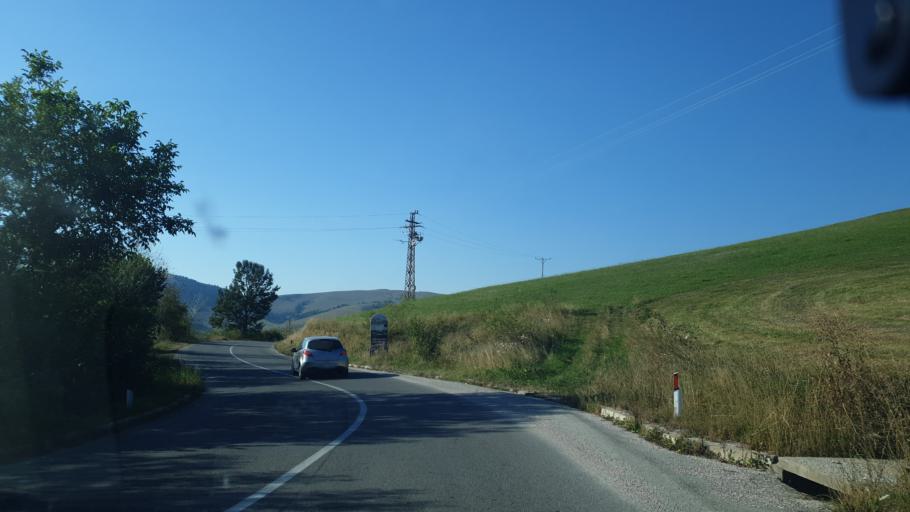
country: RS
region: Central Serbia
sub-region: Zlatiborski Okrug
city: Cajetina
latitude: 43.7150
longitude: 19.7631
